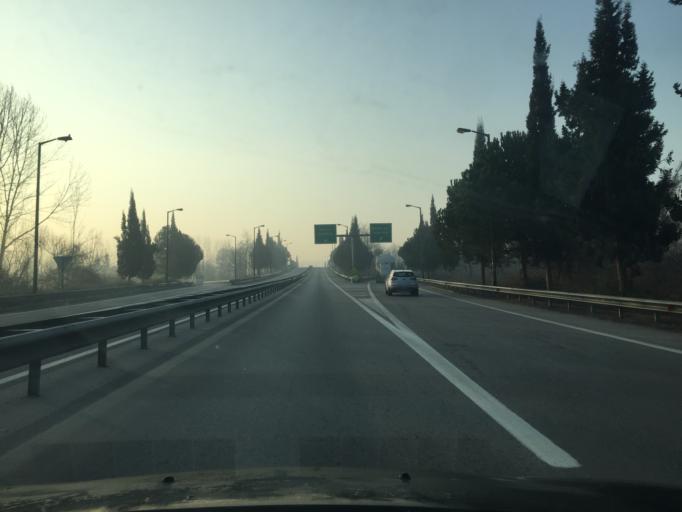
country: TR
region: Sakarya
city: Akyazi
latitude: 40.7197
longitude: 30.5679
